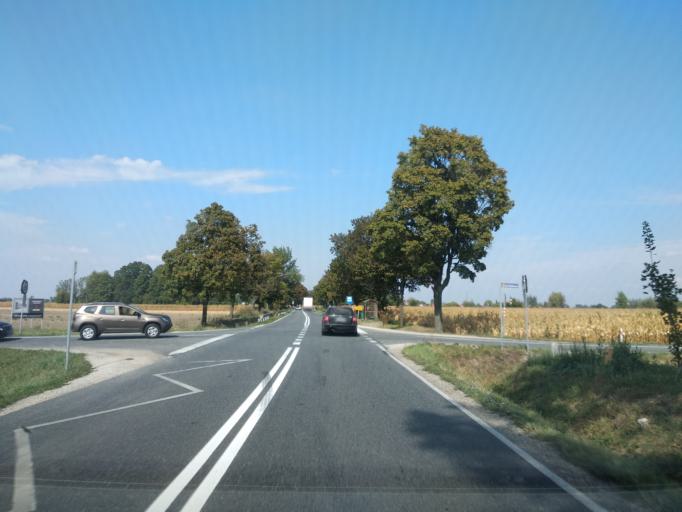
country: PL
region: Lower Silesian Voivodeship
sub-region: Powiat wroclawski
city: Zorawina
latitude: 50.9326
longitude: 17.0694
